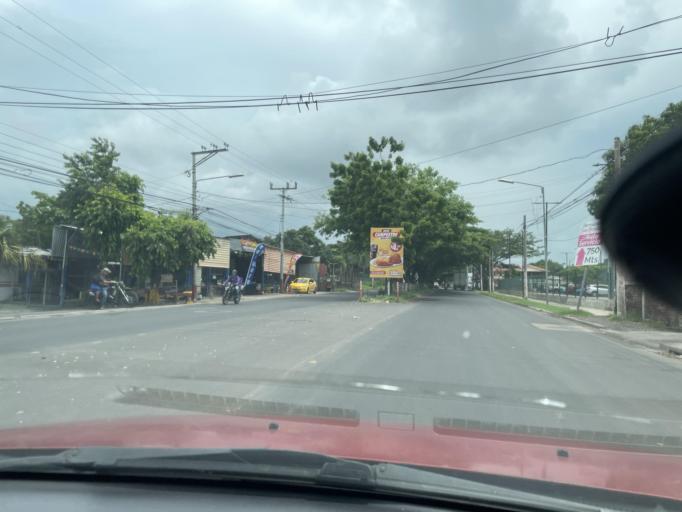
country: SV
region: San Miguel
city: San Miguel
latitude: 13.4537
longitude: -88.1591
